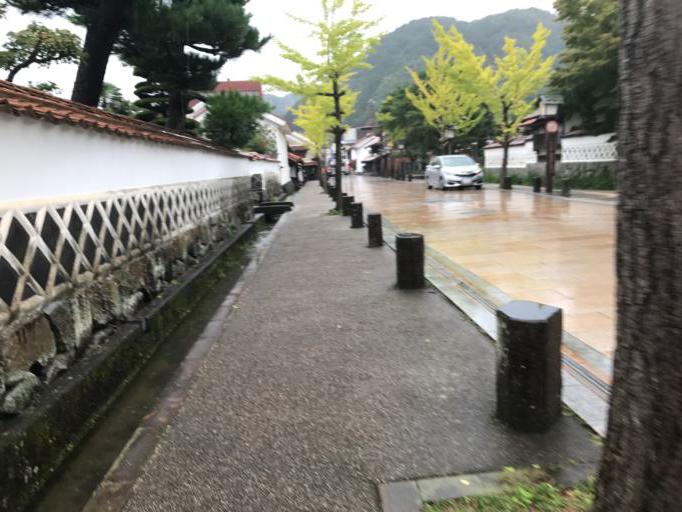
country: JP
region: Shimane
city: Masuda
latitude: 34.4673
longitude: 131.7735
